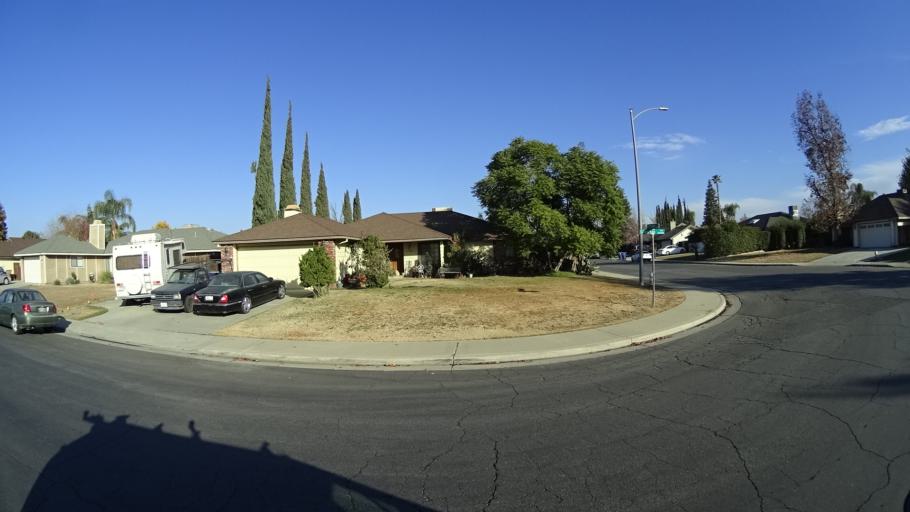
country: US
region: California
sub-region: Kern County
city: Rosedale
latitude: 35.3527
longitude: -119.1508
